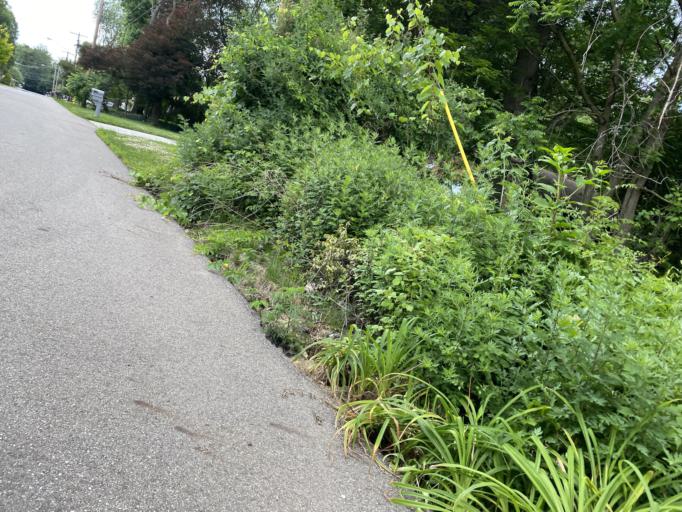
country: US
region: Ohio
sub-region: Summit County
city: Fairlawn
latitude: 41.1053
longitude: -81.5826
